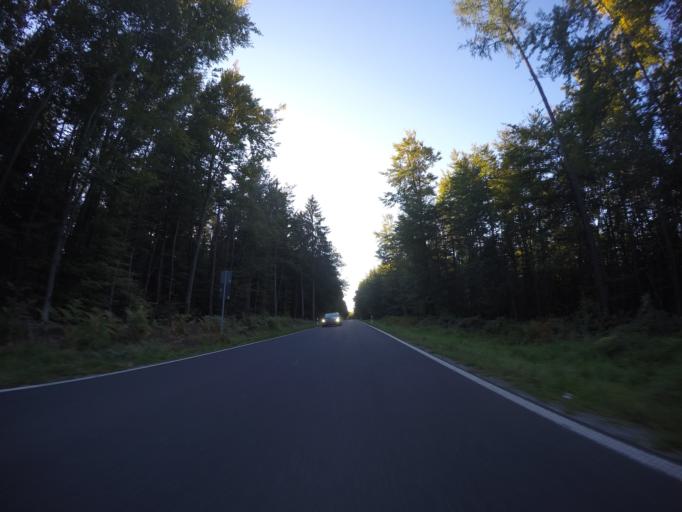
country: DE
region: Bavaria
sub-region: Regierungsbezirk Unterfranken
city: Altenbuch
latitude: 49.8664
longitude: 9.4135
